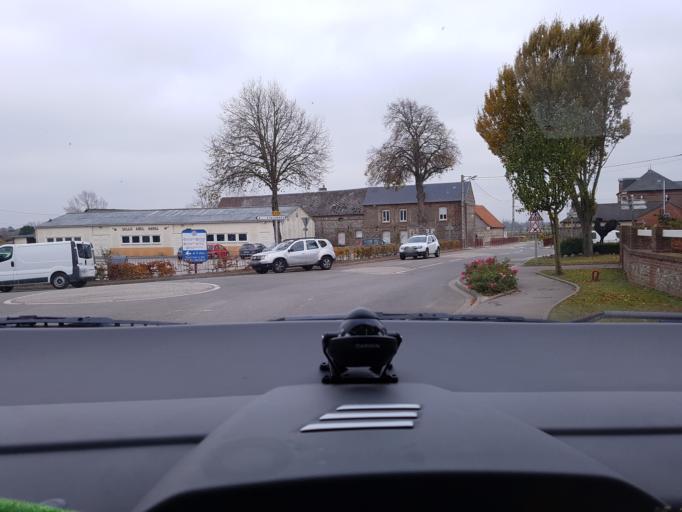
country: FR
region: Haute-Normandie
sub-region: Departement de la Seine-Maritime
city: Le Treport
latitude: 50.0379
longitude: 1.3637
